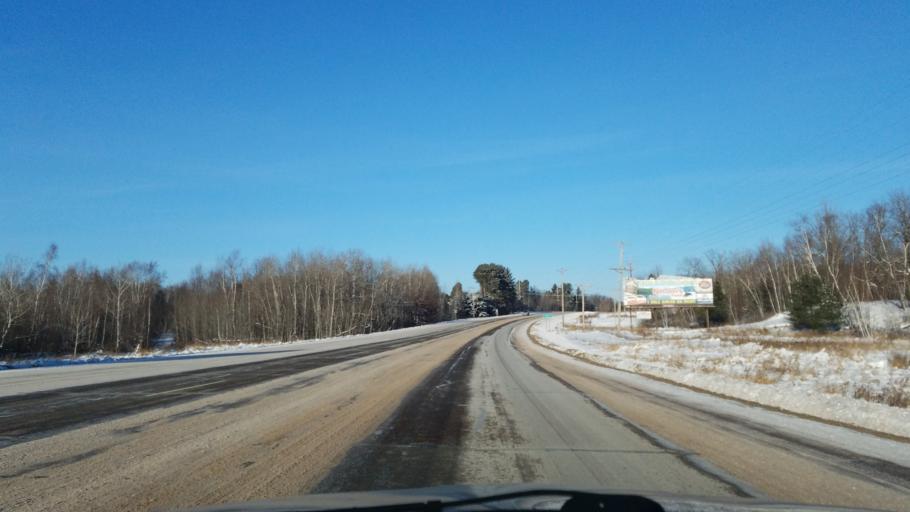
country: US
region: Wisconsin
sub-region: Barron County
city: Cumberland
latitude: 45.5211
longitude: -92.0519
